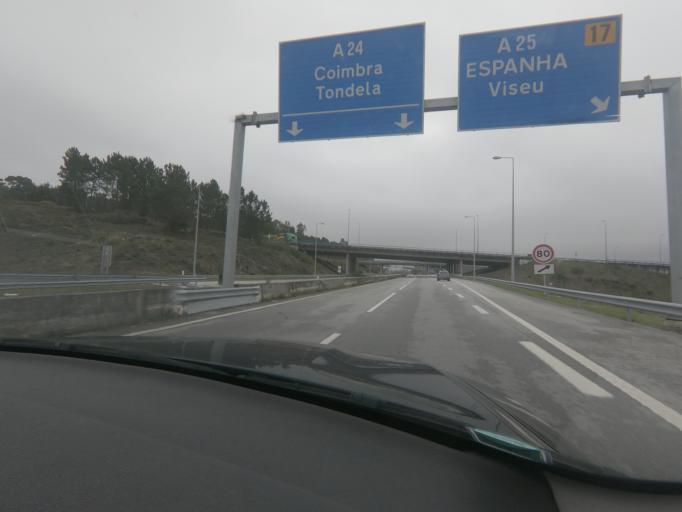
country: PT
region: Viseu
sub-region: Viseu
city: Viseu
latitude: 40.6266
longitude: -7.9614
